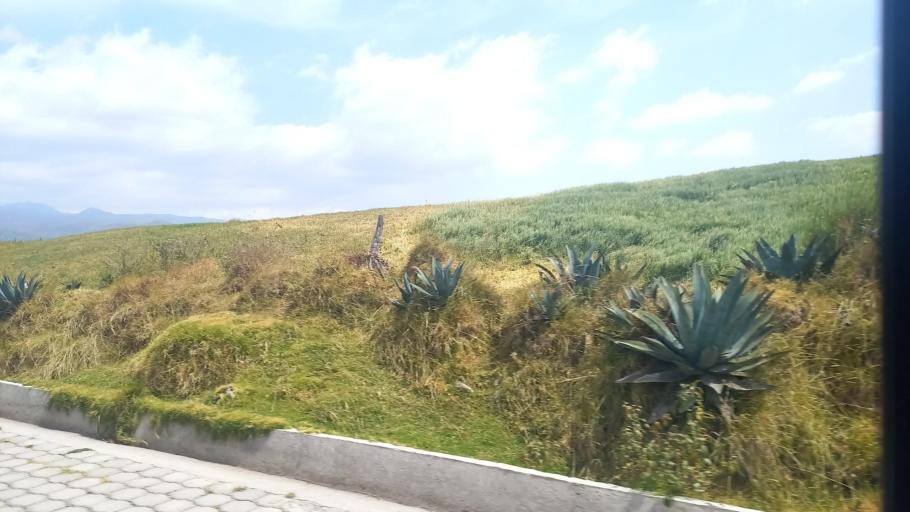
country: EC
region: Pichincha
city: Cayambe
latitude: 0.1595
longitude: -78.0761
